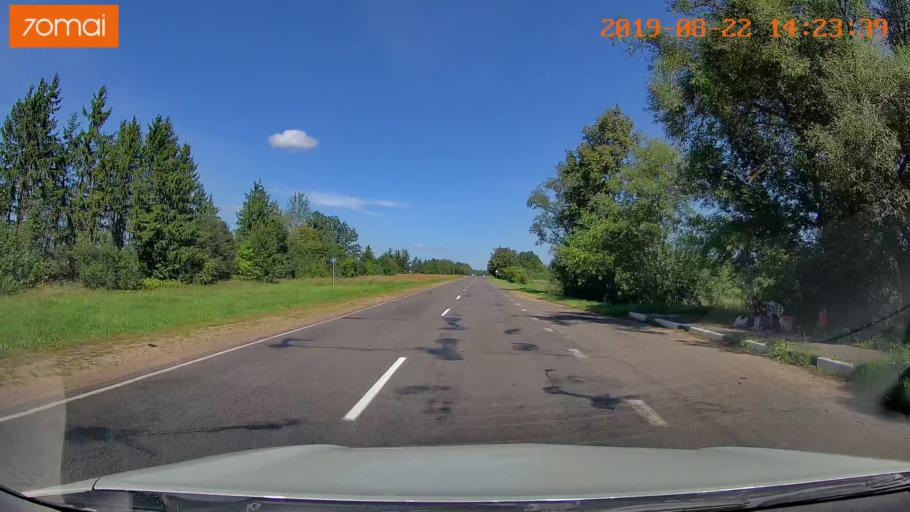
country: BY
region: Mogilev
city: Asipovichy
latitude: 53.2912
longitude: 28.5868
